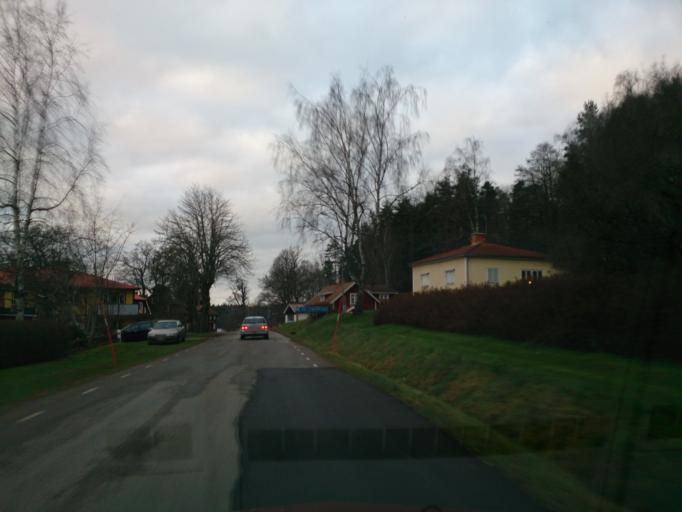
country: SE
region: OEstergoetland
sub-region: Atvidabergs Kommun
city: Atvidaberg
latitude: 58.3365
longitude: 16.0281
